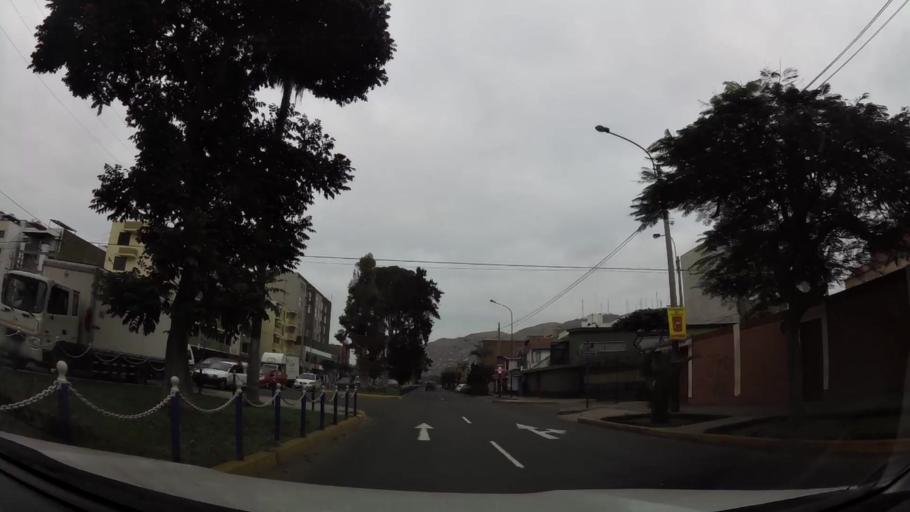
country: PE
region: Lima
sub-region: Lima
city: Surco
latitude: -12.1797
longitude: -77.0106
